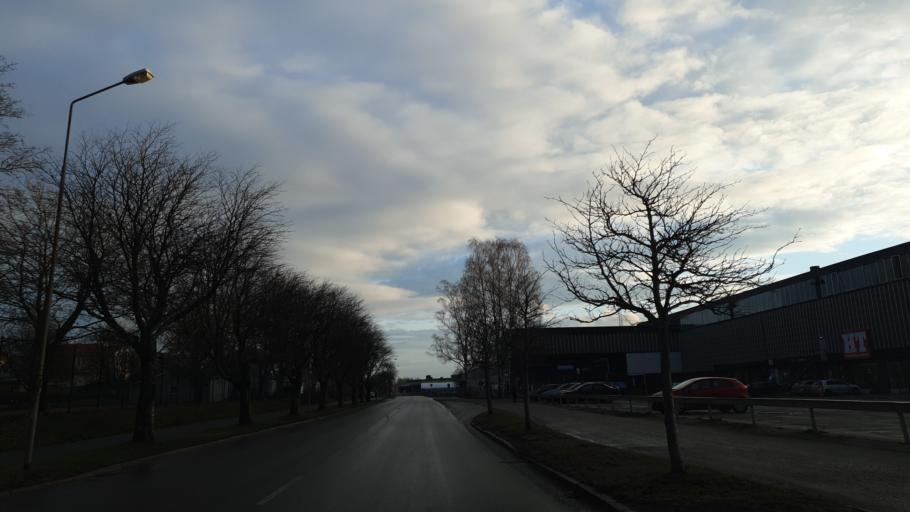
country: SE
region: Gaevleborg
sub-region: Hudiksvalls Kommun
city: Hudiksvall
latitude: 61.7254
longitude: 17.1276
